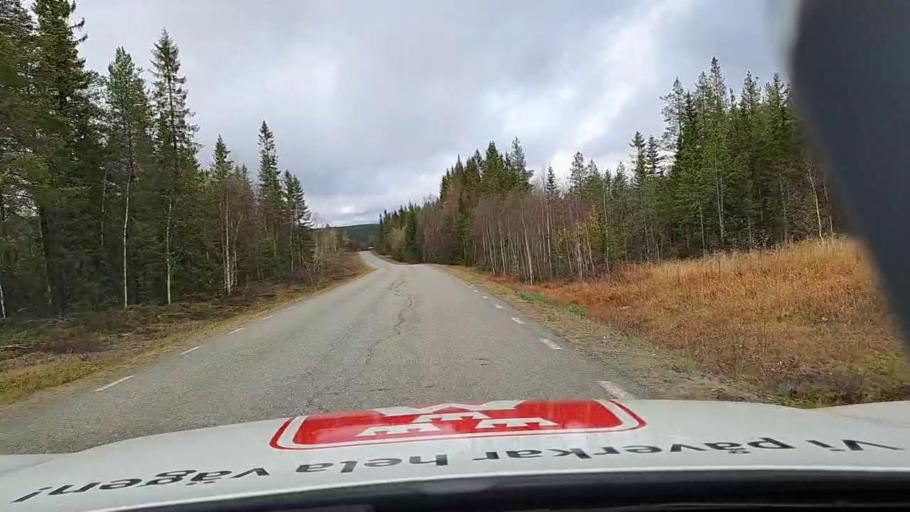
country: SE
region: Jaemtland
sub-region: Bergs Kommun
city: Hoverberg
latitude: 63.0392
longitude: 14.0169
